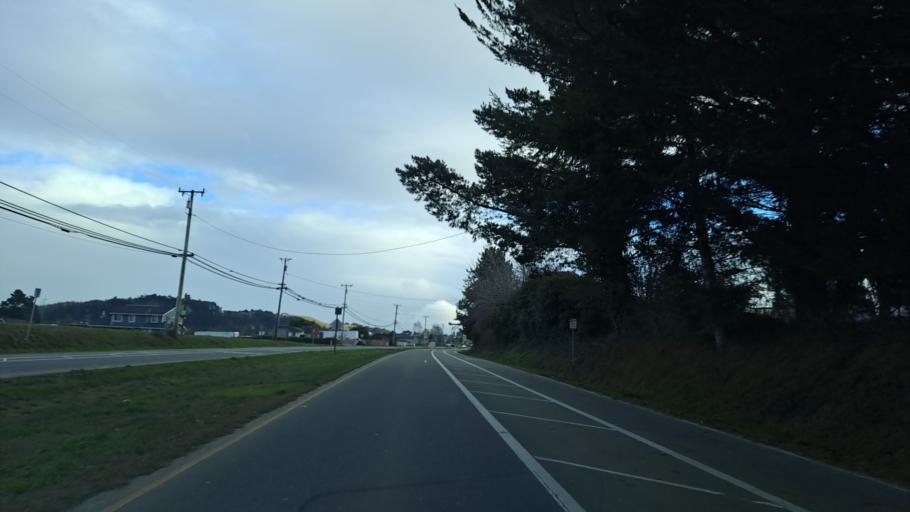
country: US
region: California
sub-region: Humboldt County
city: Fortuna
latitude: 40.5753
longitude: -124.1447
